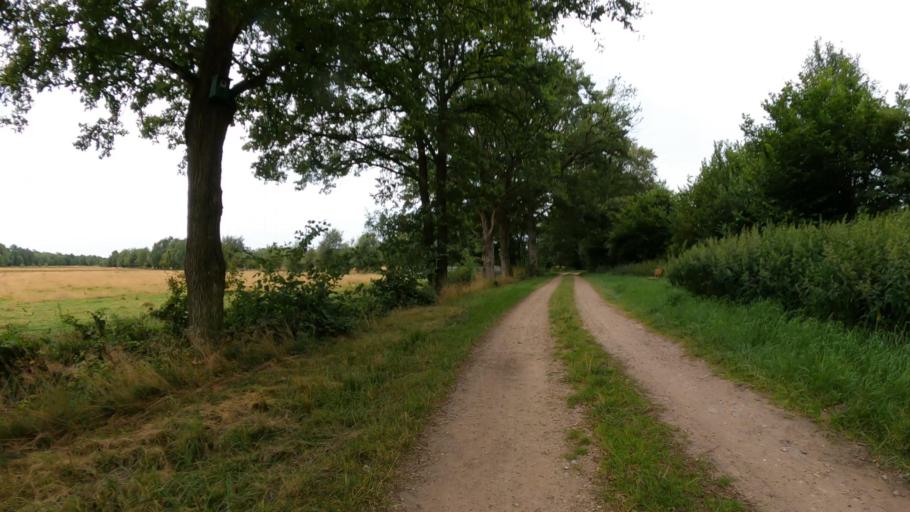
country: DE
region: Schleswig-Holstein
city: Seth
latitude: 53.8534
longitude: 10.2131
